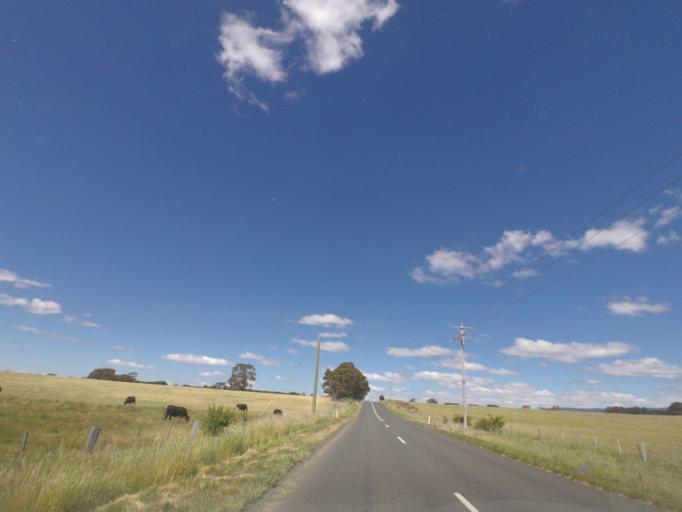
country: AU
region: Victoria
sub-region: Mount Alexander
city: Castlemaine
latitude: -37.2906
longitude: 144.4832
